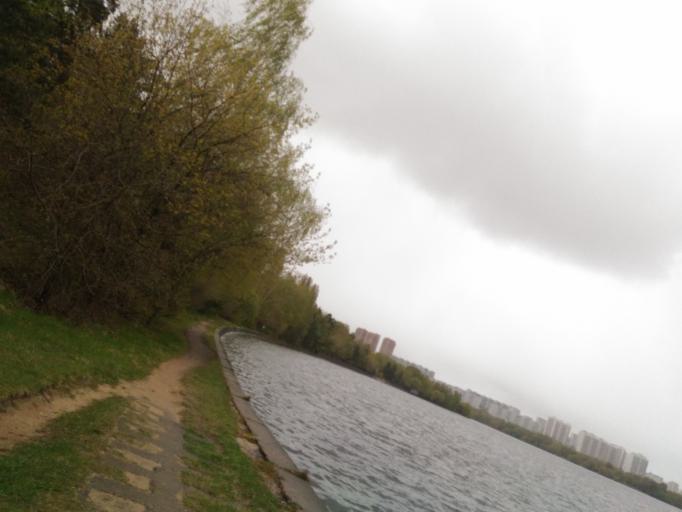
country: RU
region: Moscow
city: Shchukino
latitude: 55.7859
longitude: 37.4241
